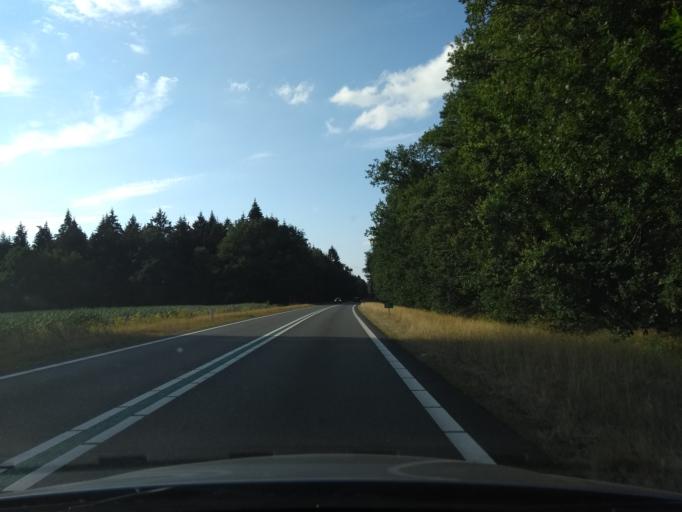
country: NL
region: Overijssel
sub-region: Gemeente Twenterand
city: Magele
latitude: 52.5375
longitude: 6.5462
